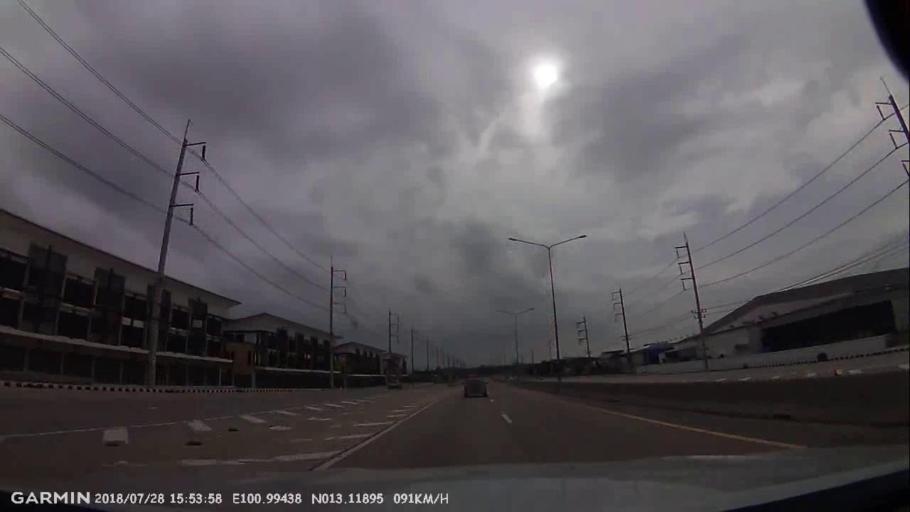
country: TH
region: Chon Buri
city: Ban Talat Bueng
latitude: 13.1189
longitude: 100.9942
